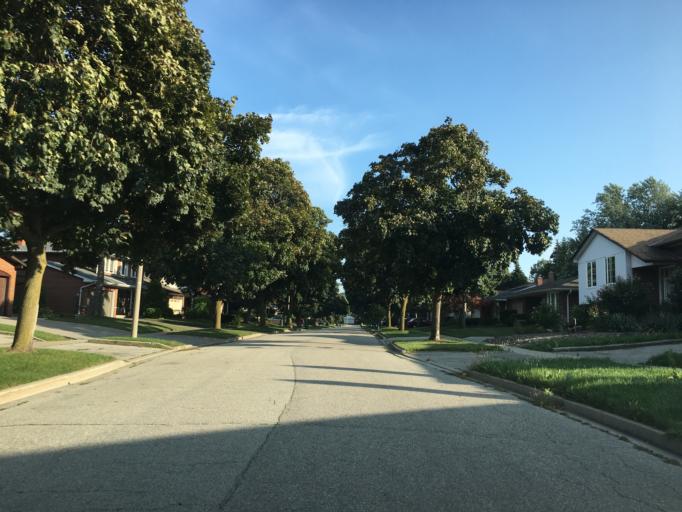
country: CA
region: Ontario
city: Scarborough
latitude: 43.7920
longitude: -79.2829
